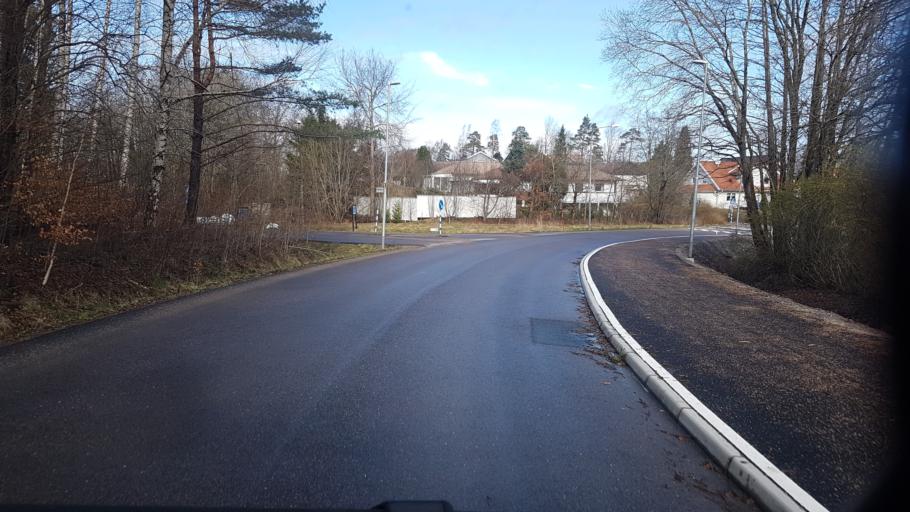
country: SE
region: Vaestra Goetaland
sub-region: Lerums Kommun
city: Stenkullen
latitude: 57.8095
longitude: 12.3715
